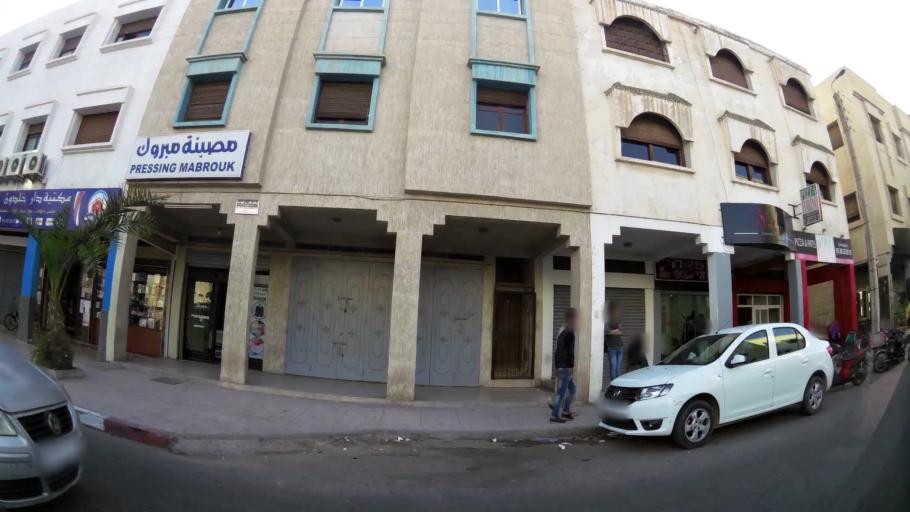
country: MA
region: Oued ed Dahab-Lagouira
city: Dakhla
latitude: 30.4106
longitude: -9.5567
